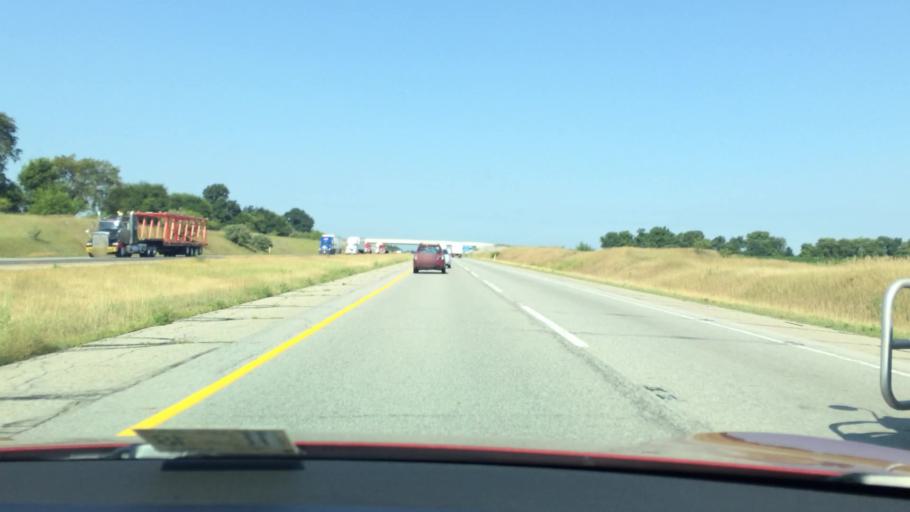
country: US
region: Michigan
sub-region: Branch County
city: Bronson
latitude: 41.7556
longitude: -85.1371
